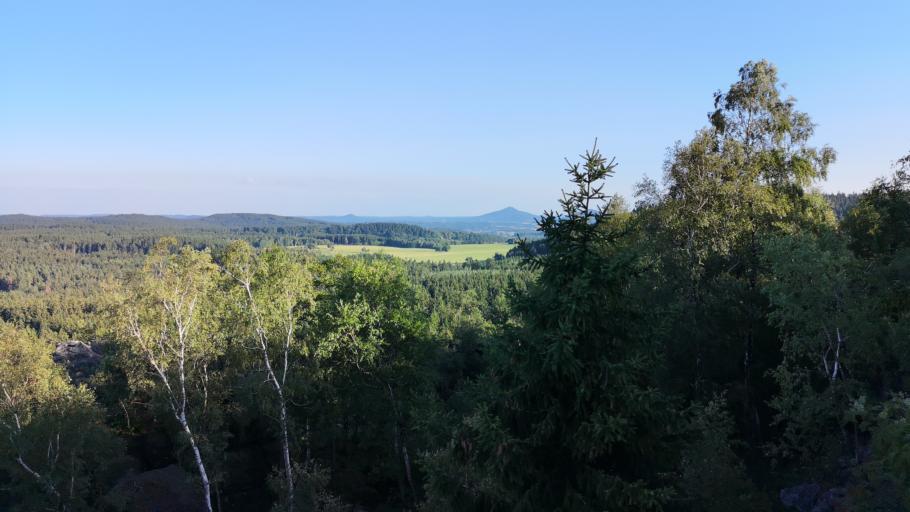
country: DE
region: Saxony
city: Kurort Oybin
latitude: 50.8470
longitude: 14.7666
